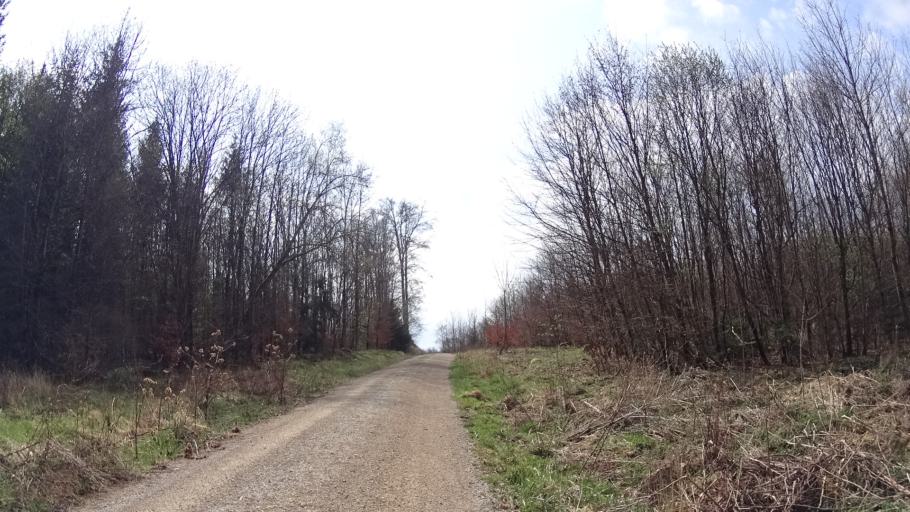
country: DE
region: Bavaria
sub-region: Upper Bavaria
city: Bohmfeld
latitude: 48.8945
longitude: 11.3734
